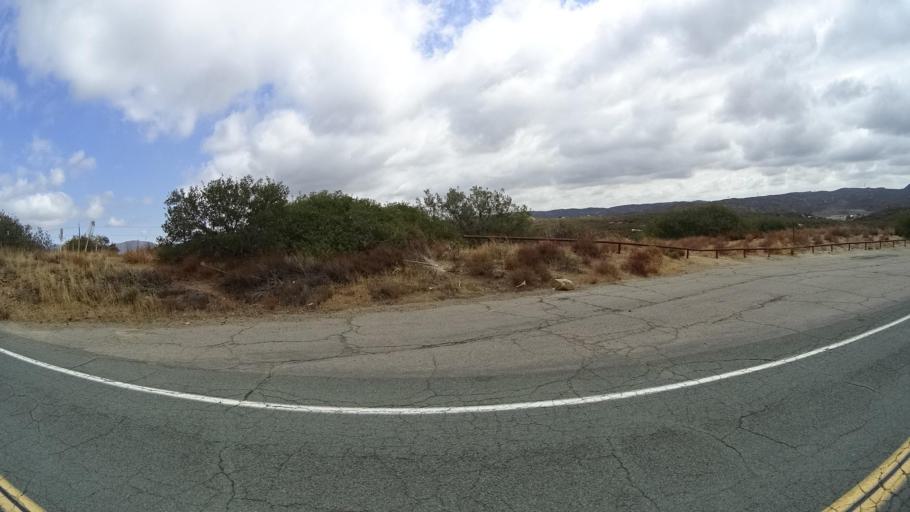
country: US
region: California
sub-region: San Diego County
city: Pine Valley
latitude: 32.7353
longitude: -116.4537
